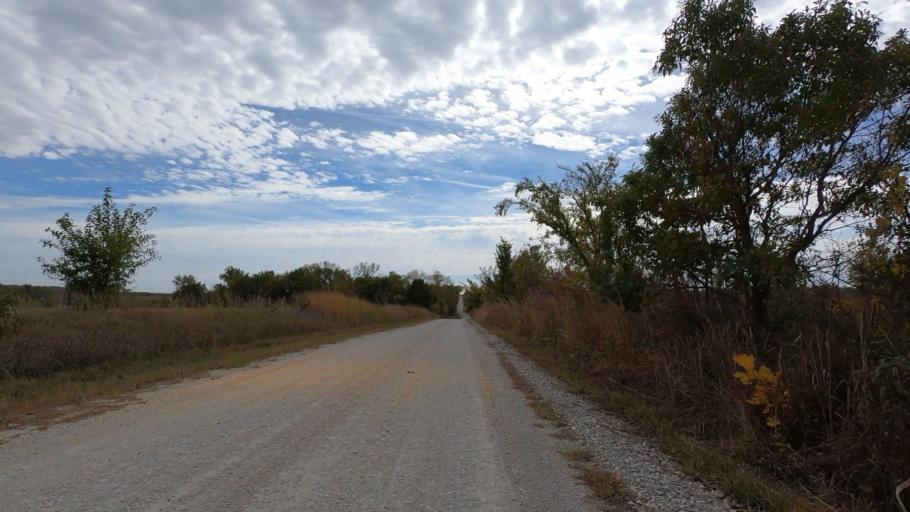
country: US
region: Kansas
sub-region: Pottawatomie County
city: Westmoreland
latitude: 39.3440
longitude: -96.4453
